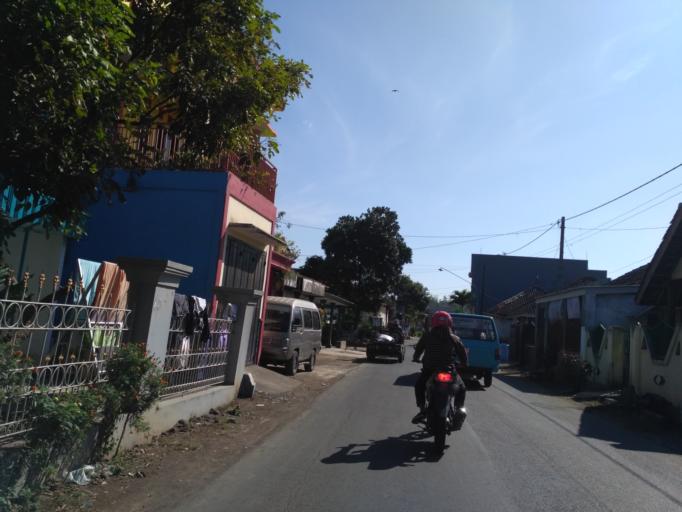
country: ID
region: East Java
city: Singosari
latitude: -7.9249
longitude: 112.6666
